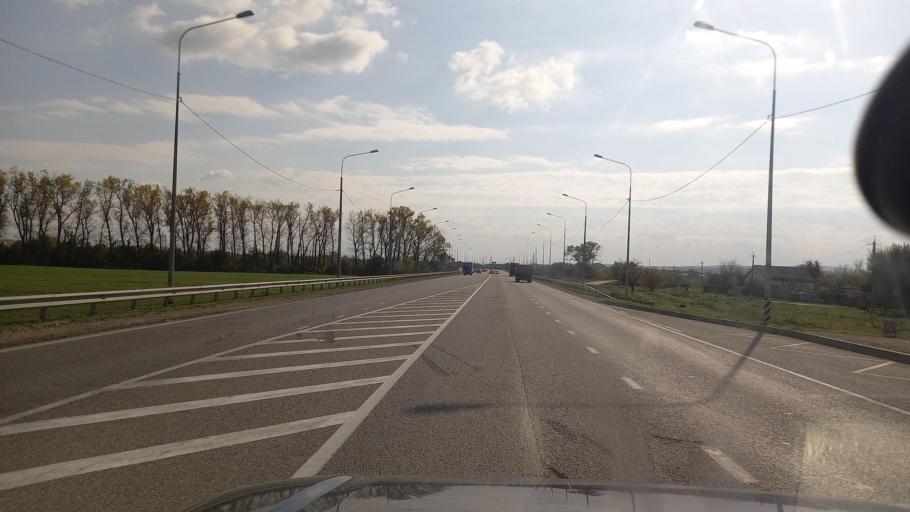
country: RU
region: Krasnodarskiy
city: Novoukrainskiy
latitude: 44.9023
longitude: 38.0348
